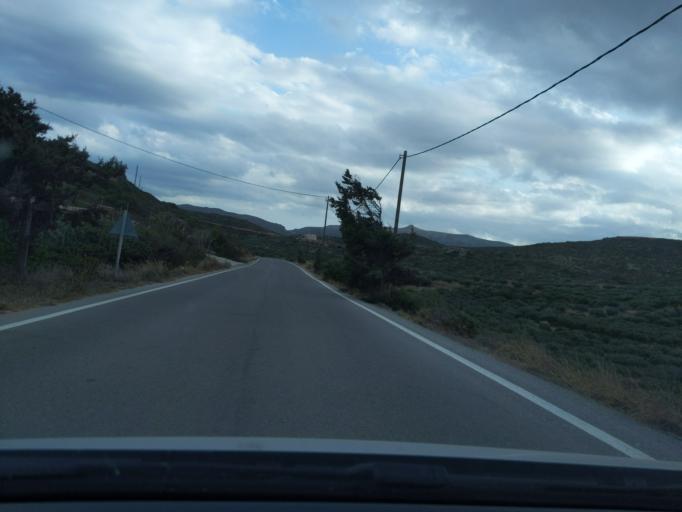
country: GR
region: Crete
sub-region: Nomos Lasithiou
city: Palekastro
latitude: 35.2268
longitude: 26.2561
